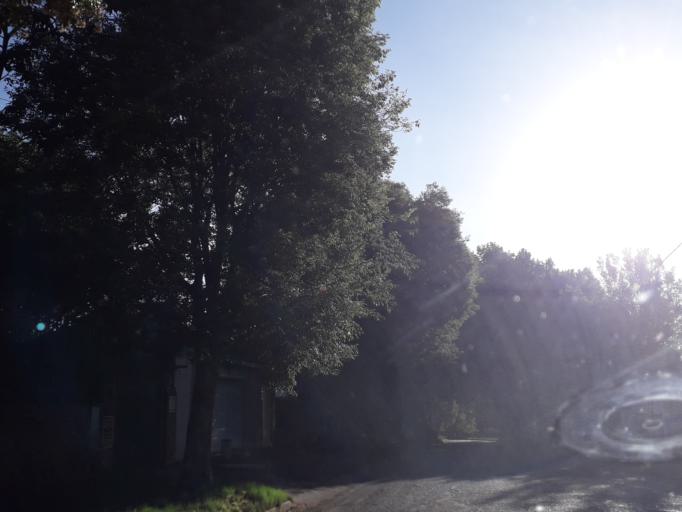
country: ZA
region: Gauteng
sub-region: City of Johannesburg Metropolitan Municipality
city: Johannesburg
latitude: -26.1587
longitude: 28.0214
